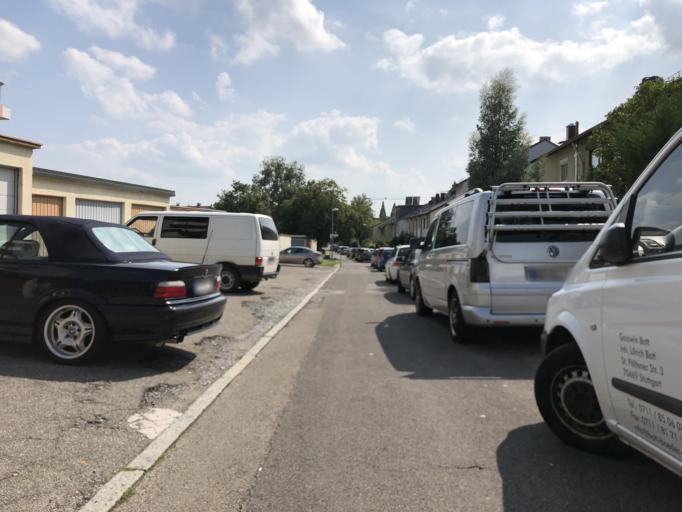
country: DE
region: Baden-Wuerttemberg
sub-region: Regierungsbezirk Stuttgart
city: Sindelfingen
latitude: 48.7253
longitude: 9.0066
